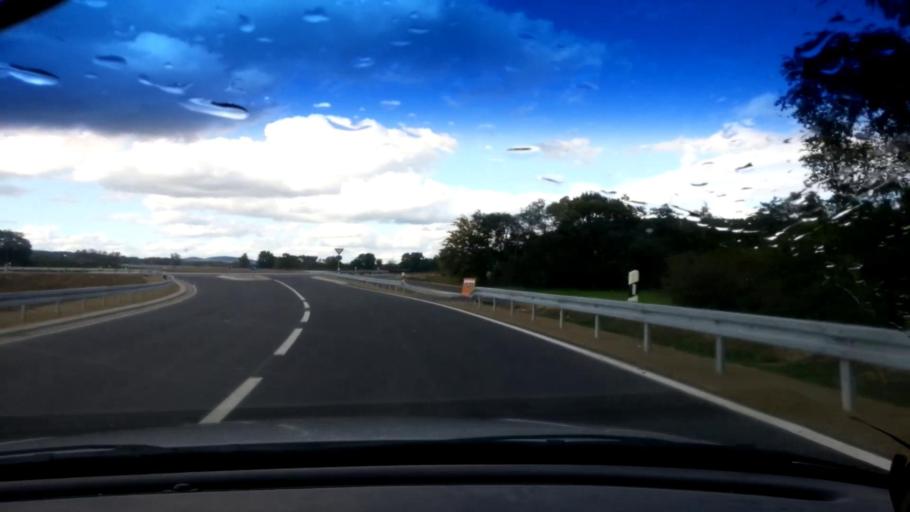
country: DE
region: Bavaria
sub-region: Upper Franconia
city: Zapfendorf
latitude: 50.0238
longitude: 10.9387
